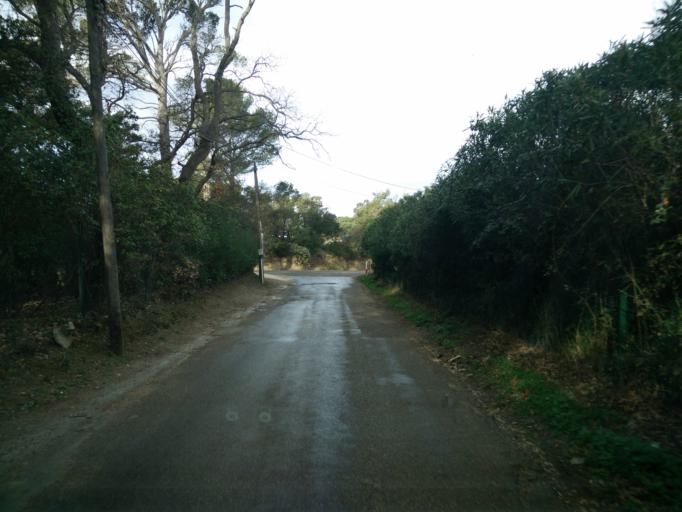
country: FR
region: Provence-Alpes-Cote d'Azur
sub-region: Departement du Var
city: Six-Fours-les-Plages
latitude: 43.0696
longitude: 5.8241
